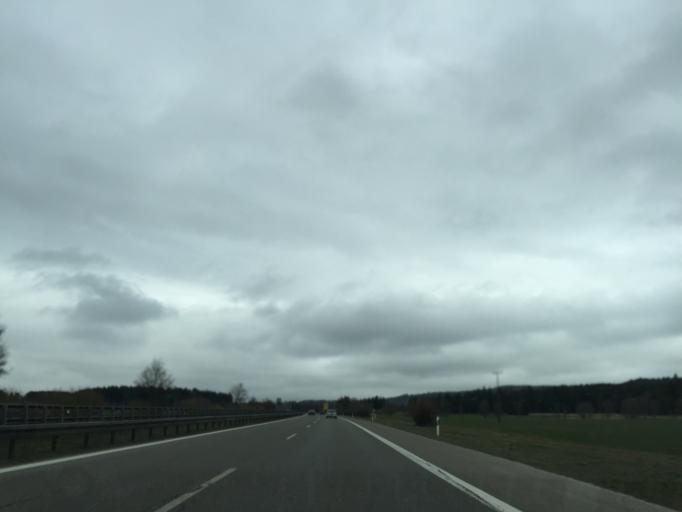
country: DE
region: Baden-Wuerttemberg
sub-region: Freiburg Region
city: Bad Durrheim
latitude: 47.9979
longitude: 8.5303
